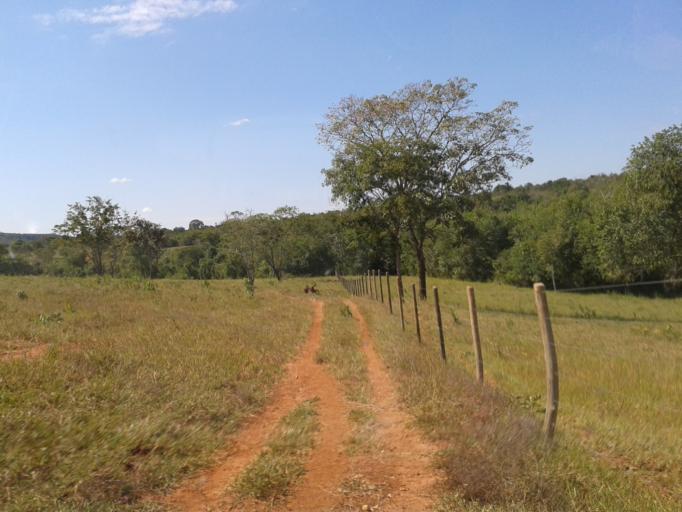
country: BR
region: Minas Gerais
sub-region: Campina Verde
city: Campina Verde
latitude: -19.4014
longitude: -49.7440
